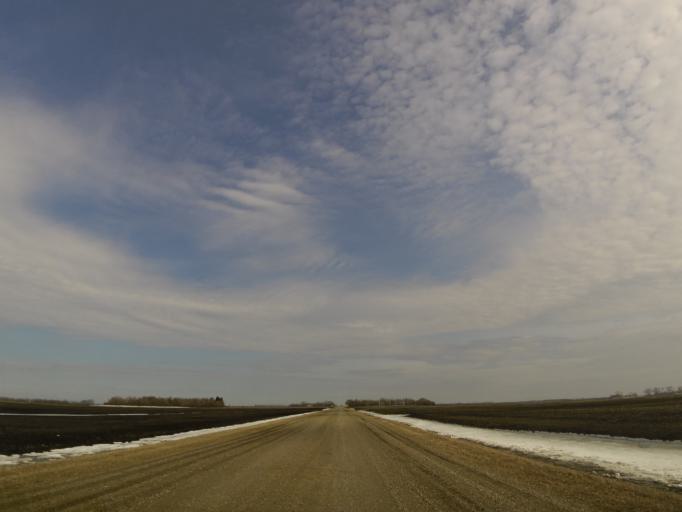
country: US
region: North Dakota
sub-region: Walsh County
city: Grafton
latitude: 48.4265
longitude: -97.2425
